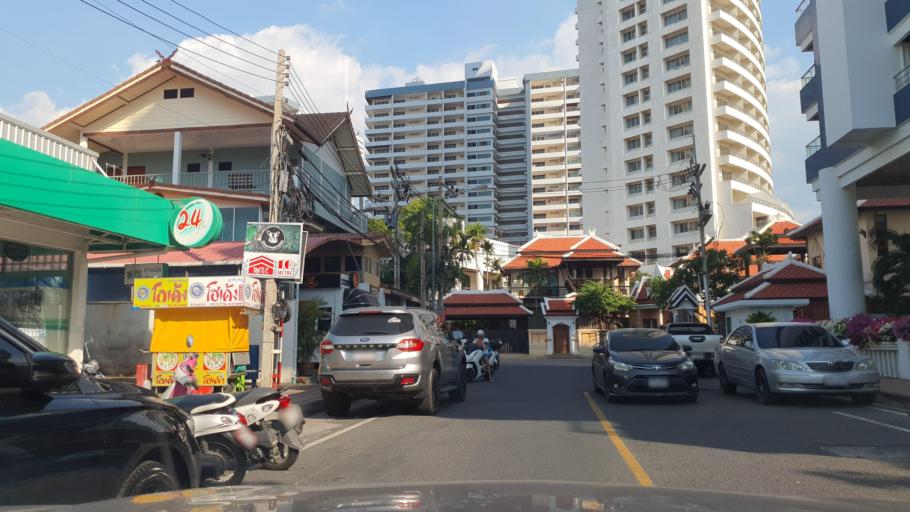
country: TH
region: Chon Buri
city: Phatthaya
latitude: 12.9089
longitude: 100.8585
